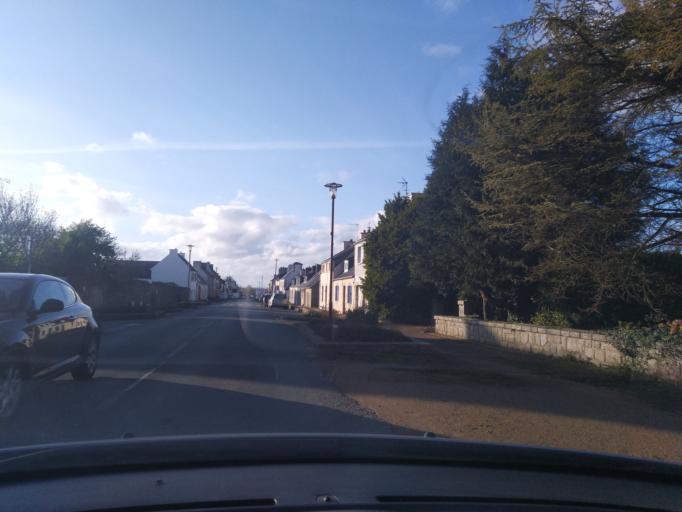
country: FR
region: Brittany
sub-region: Departement du Finistere
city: Plouigneau
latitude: 48.5693
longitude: -3.7001
